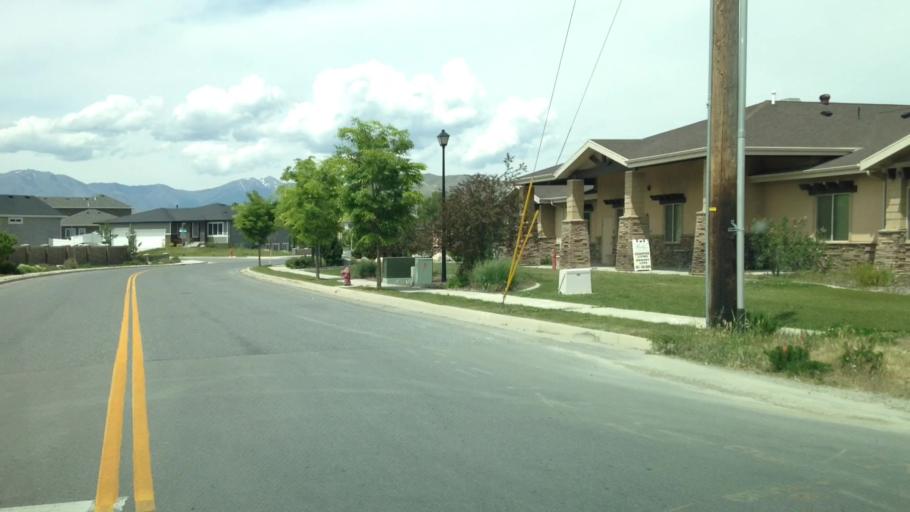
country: US
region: Utah
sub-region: Utah County
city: Lehi
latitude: 40.3912
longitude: -111.8865
